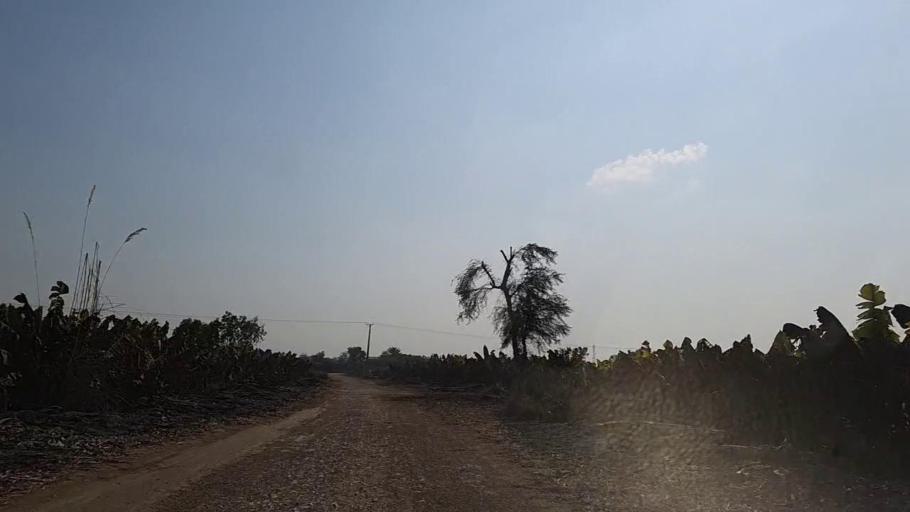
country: PK
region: Sindh
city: Daur
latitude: 26.4138
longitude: 68.2379
